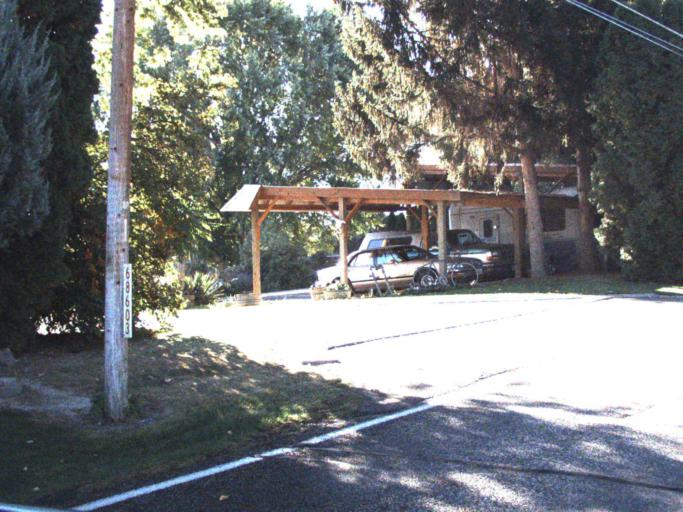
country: US
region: Washington
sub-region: Benton County
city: Benton City
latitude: 46.3130
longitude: -119.4933
